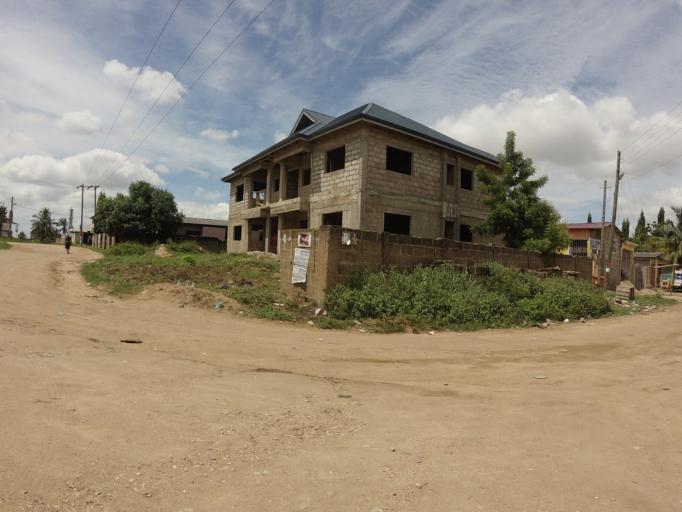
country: GH
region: Central
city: Kasoa
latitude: 5.5467
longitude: -0.4038
